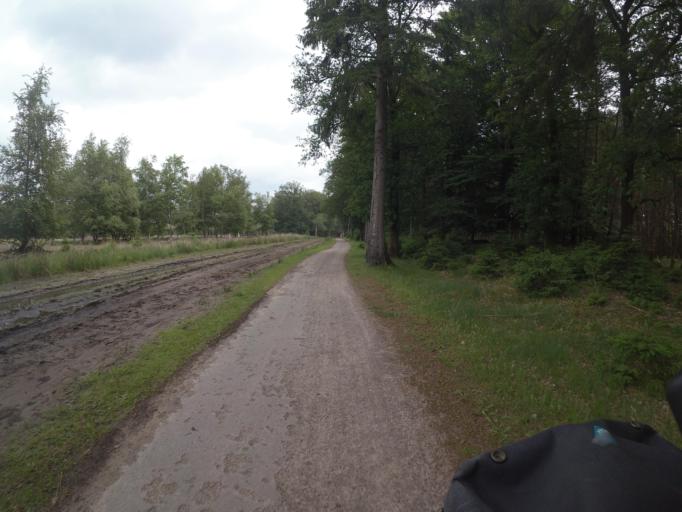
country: NL
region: Drenthe
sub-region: Gemeente Westerveld
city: Dwingeloo
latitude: 52.8130
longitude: 6.4476
